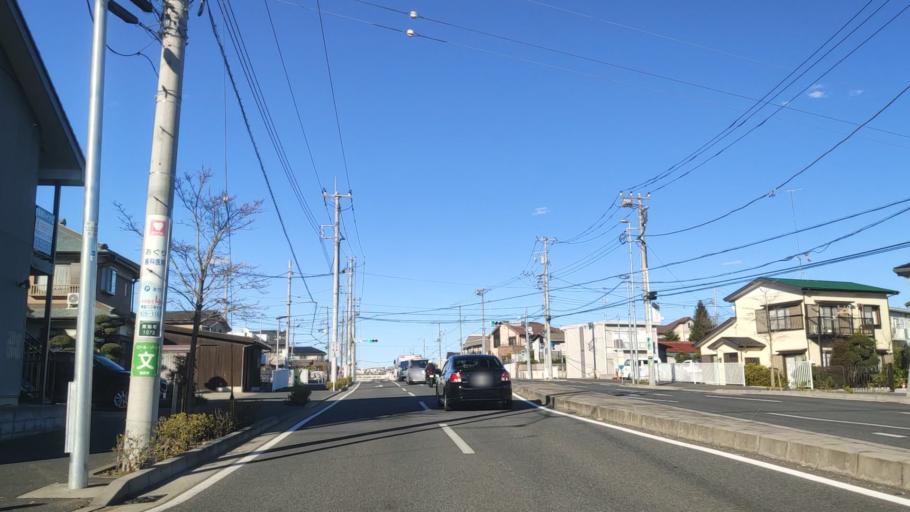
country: JP
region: Tokyo
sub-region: Machida-shi
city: Machida
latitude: 35.5194
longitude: 139.5442
